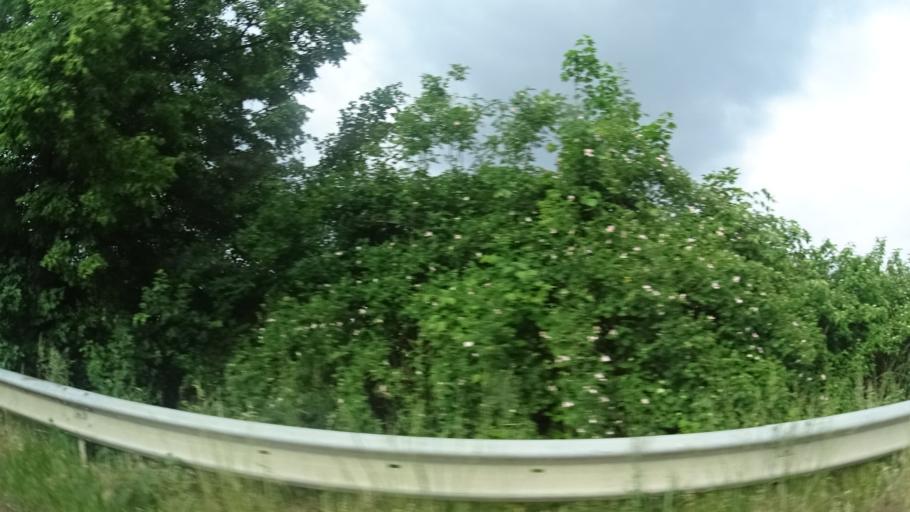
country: DE
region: Rheinland-Pfalz
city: Schifferstadt
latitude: 49.3872
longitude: 8.3670
